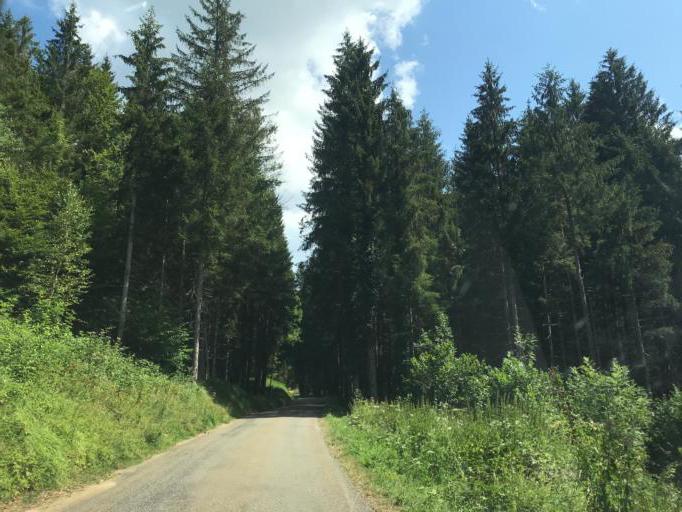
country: FR
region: Franche-Comte
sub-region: Departement du Jura
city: Moirans-en-Montagne
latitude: 46.4935
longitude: 5.7613
